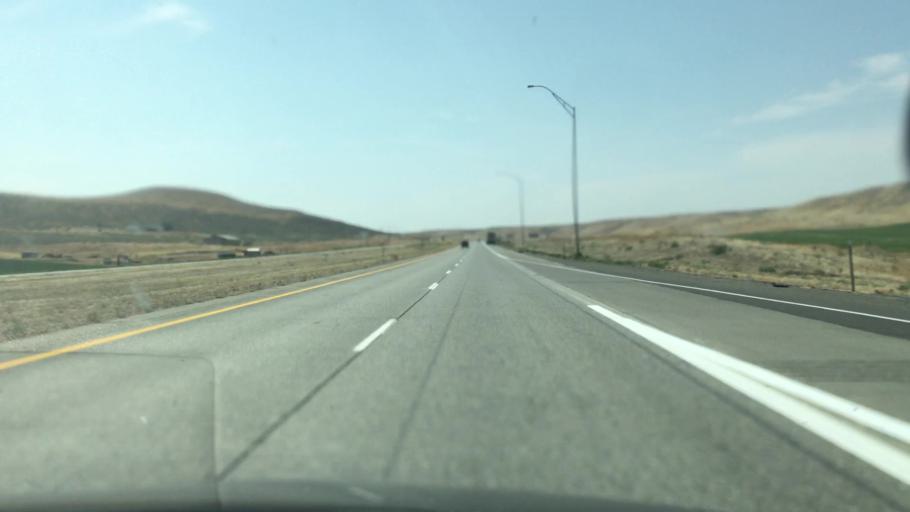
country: US
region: Idaho
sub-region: Elmore County
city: Glenns Ferry
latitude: 42.9624
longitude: -115.3142
